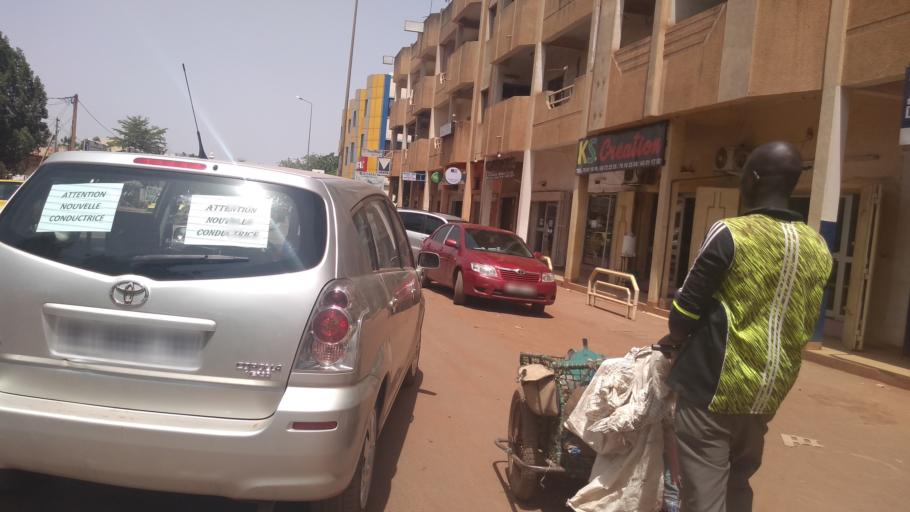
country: ML
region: Bamako
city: Bamako
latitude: 12.6417
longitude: -8.0235
